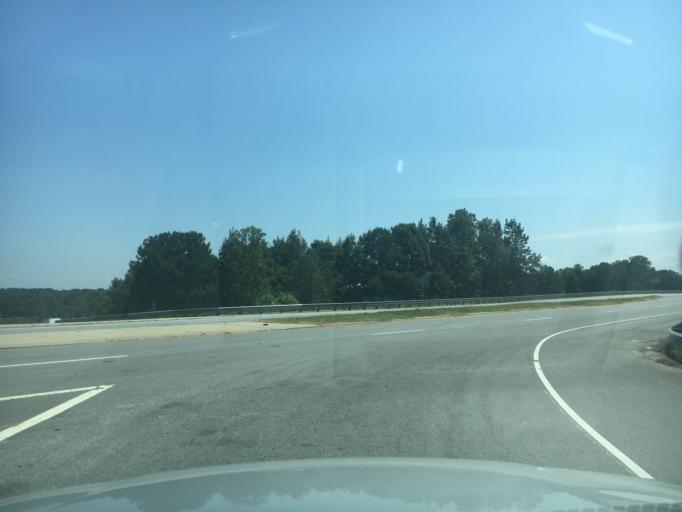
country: US
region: North Carolina
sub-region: Rutherford County
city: Spindale
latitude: 35.3066
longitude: -81.9220
